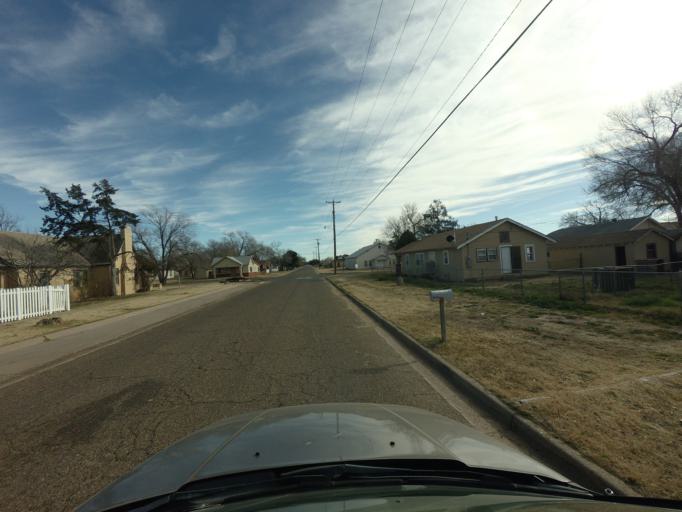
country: US
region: New Mexico
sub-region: Curry County
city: Clovis
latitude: 34.4089
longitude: -103.1996
